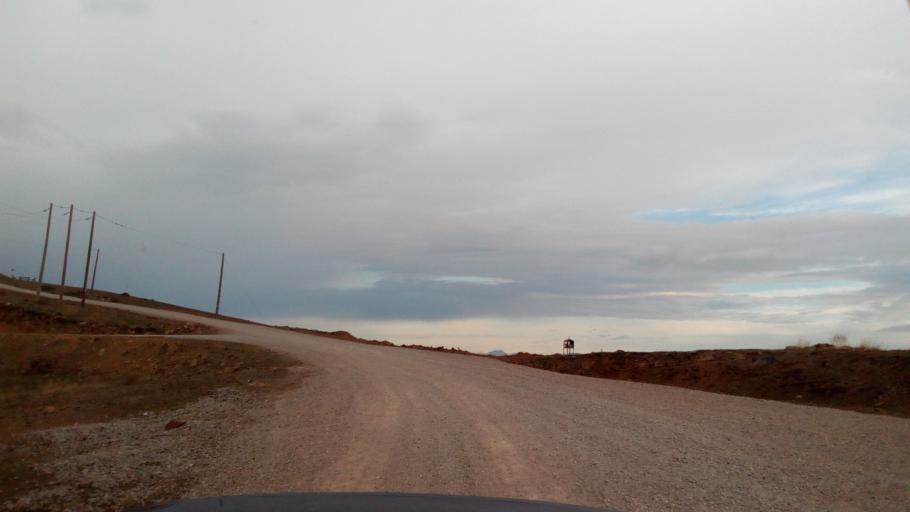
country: GR
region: Central Greece
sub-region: Nomos Fokidos
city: Lidoriki
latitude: 38.4584
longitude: 22.0727
